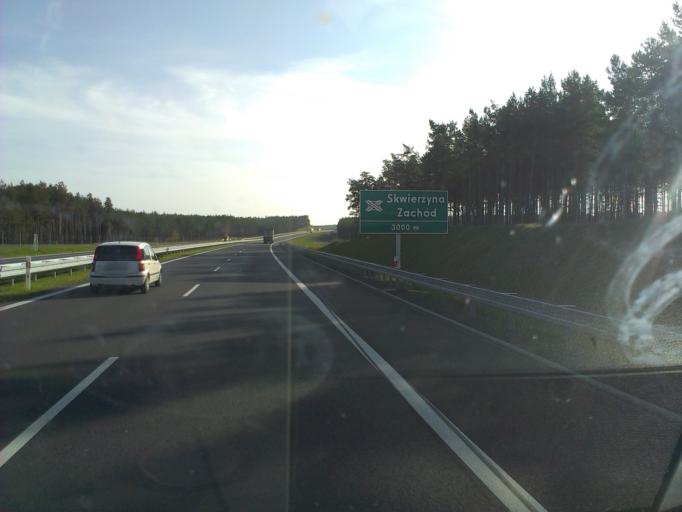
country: PL
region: Lubusz
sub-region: Powiat miedzyrzecki
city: Bledzew
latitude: 52.6095
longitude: 15.4139
